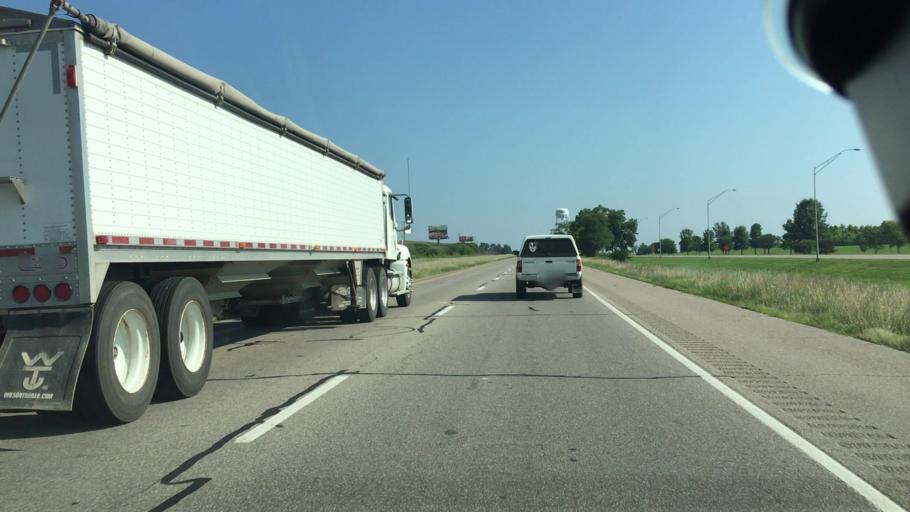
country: US
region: Indiana
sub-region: Gibson County
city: Fort Branch
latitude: 38.2818
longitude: -87.5675
